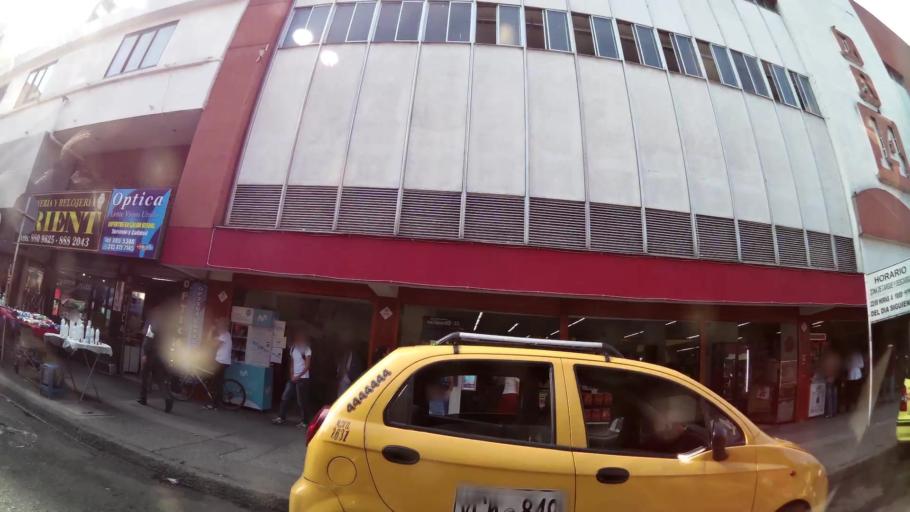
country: CO
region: Valle del Cauca
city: Cali
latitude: 3.4527
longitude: -76.5299
